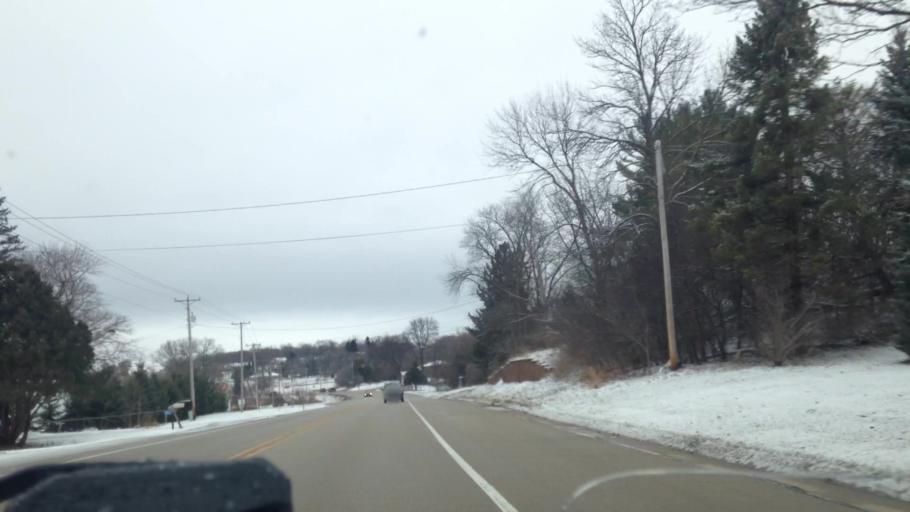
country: US
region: Wisconsin
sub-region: Dodge County
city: Beaver Dam
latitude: 43.4514
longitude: -88.8003
